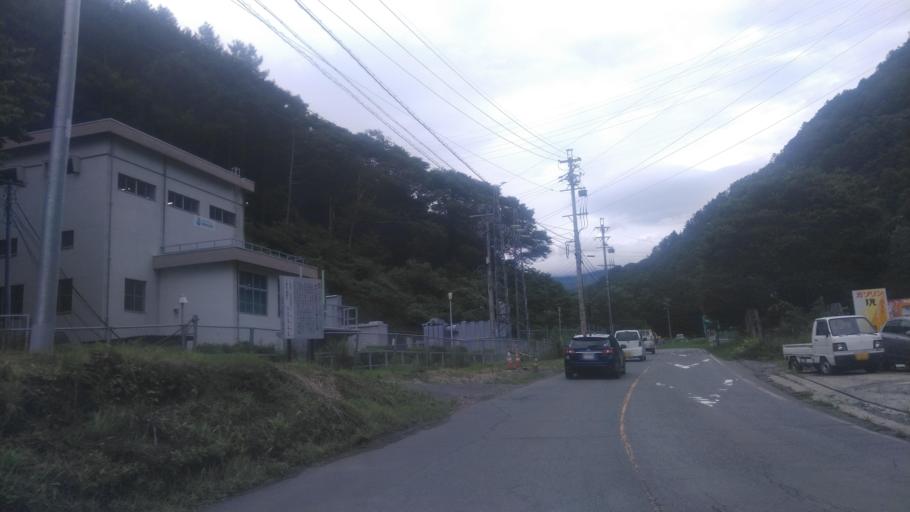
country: JP
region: Nagano
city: Ueda
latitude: 36.4652
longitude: 138.3401
